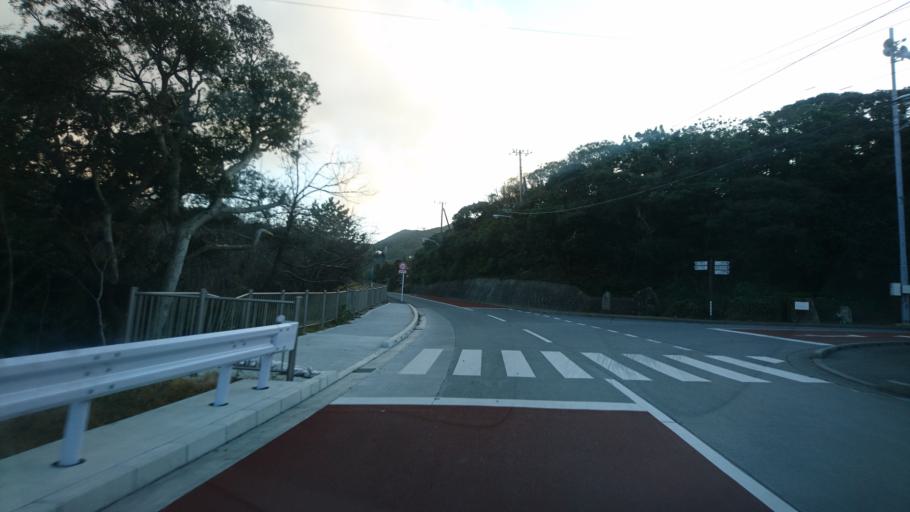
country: JP
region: Shizuoka
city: Shimoda
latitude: 34.3679
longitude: 139.2587
